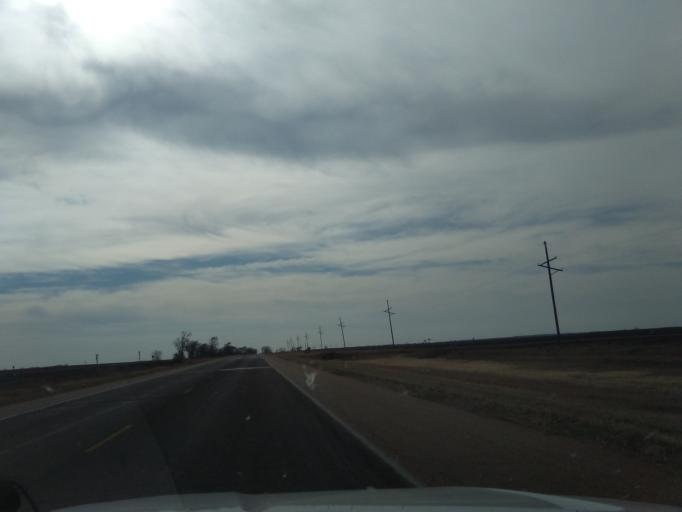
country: US
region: Nebraska
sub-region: Jefferson County
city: Fairbury
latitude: 40.1741
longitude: -97.1038
